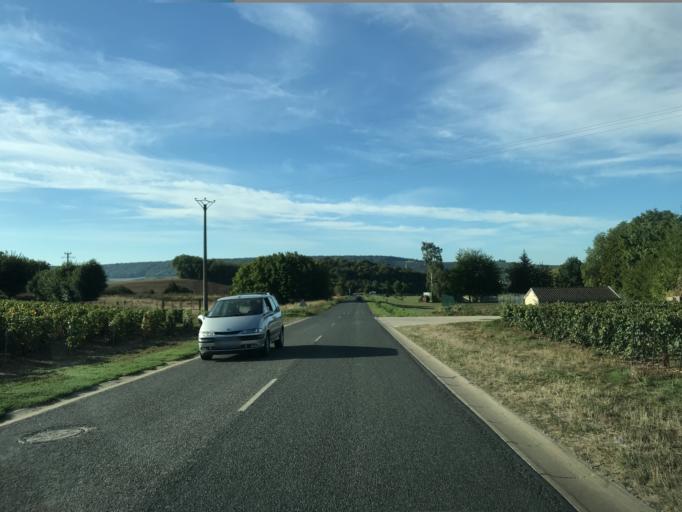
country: FR
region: Champagne-Ardenne
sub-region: Departement de la Marne
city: Chatillon-sur-Marne
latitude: 49.0984
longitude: 3.7672
